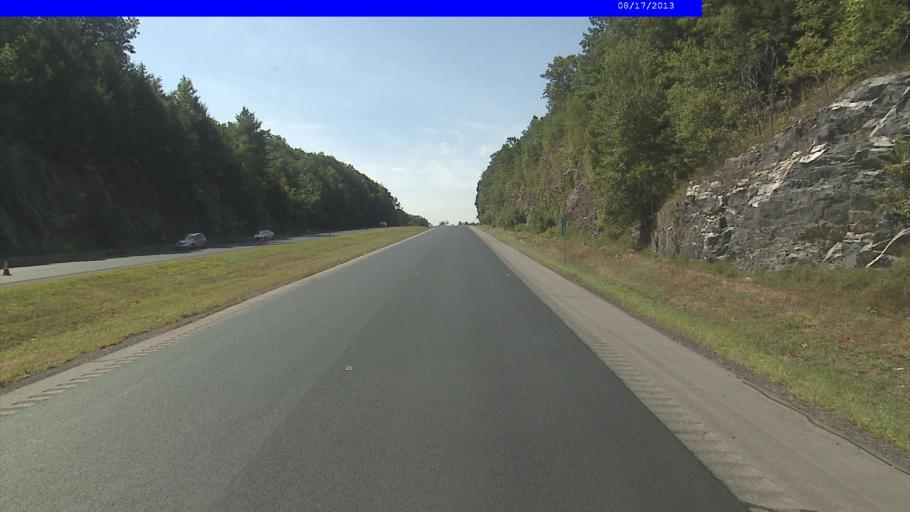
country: US
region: Vermont
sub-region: Windham County
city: Brattleboro
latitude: 42.9021
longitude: -72.5371
